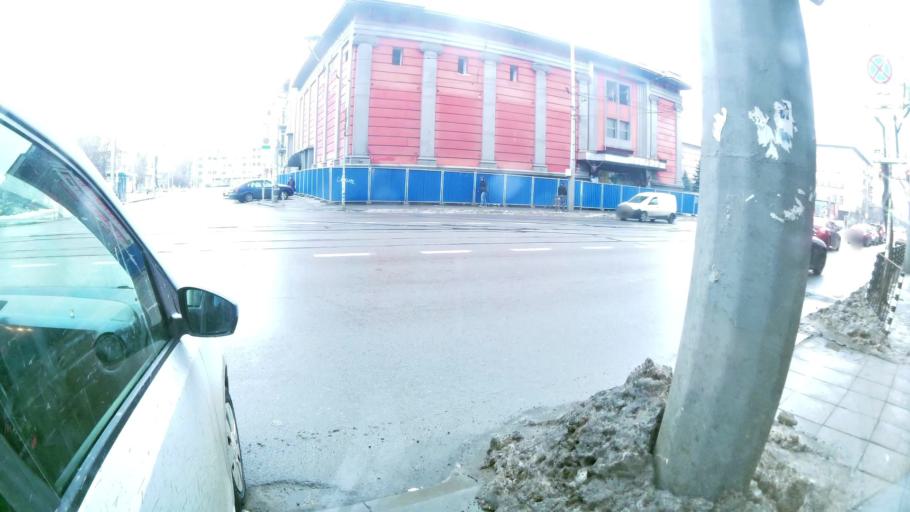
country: BG
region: Sofia-Capital
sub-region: Stolichna Obshtina
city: Sofia
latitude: 42.7132
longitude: 23.3381
